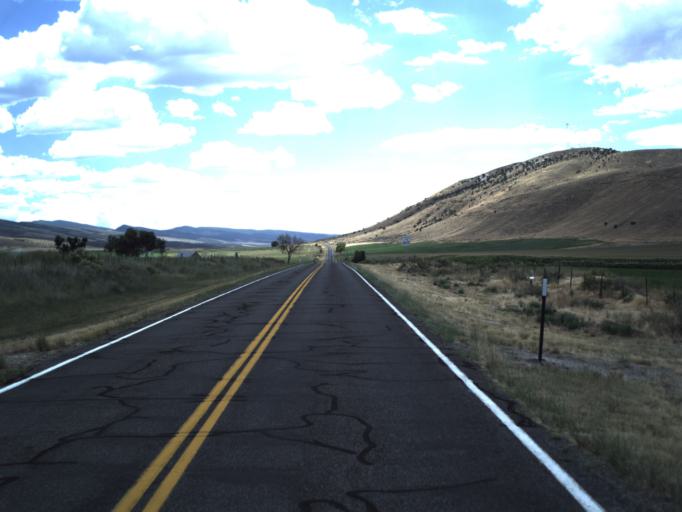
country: US
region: Utah
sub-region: Sanpete County
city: Gunnison
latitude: 39.1679
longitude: -111.7054
